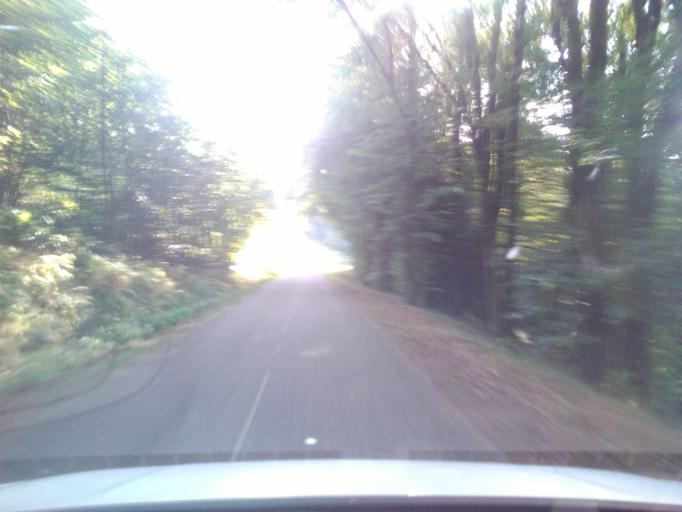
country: FR
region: Lorraine
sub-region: Departement des Vosges
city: Senones
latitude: 48.3813
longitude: 7.0453
